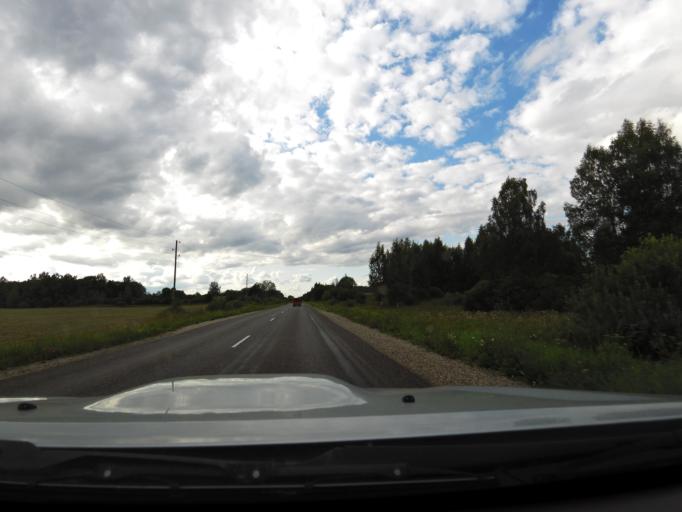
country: LV
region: Akniste
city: Akniste
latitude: 55.9920
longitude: 25.9752
